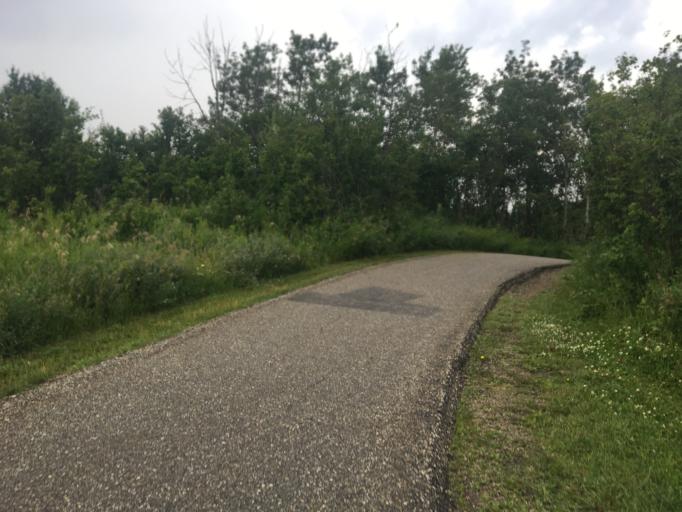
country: CA
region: Alberta
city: Grande Prairie
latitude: 55.1569
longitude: -118.8038
